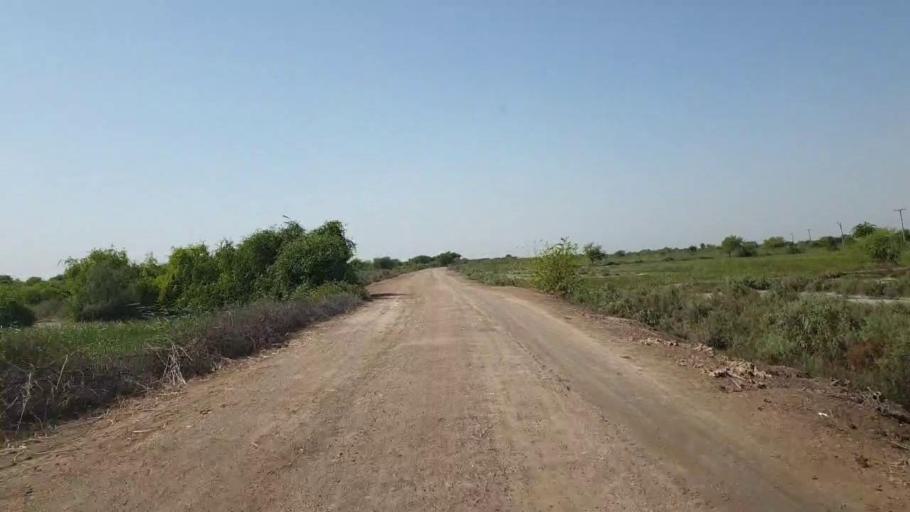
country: PK
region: Sindh
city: Tando Bago
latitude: 24.7048
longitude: 69.0353
